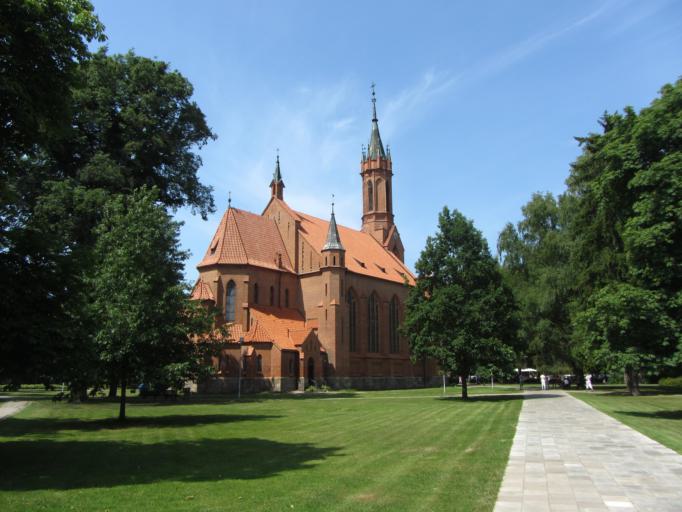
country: LT
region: Alytaus apskritis
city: Druskininkai
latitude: 54.0167
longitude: 23.9753
